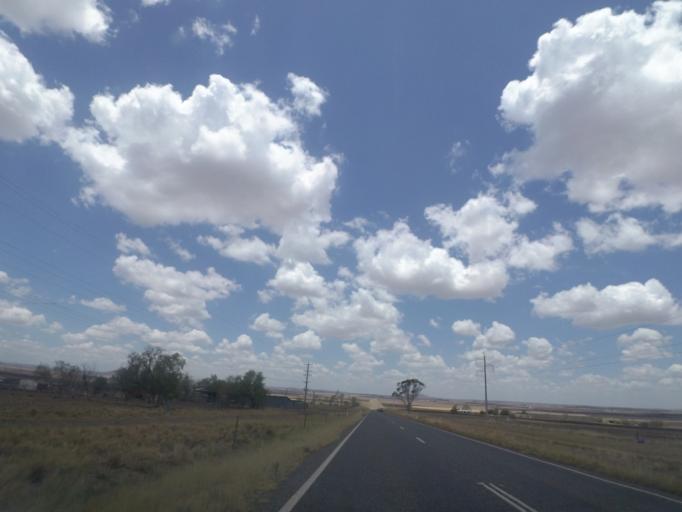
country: AU
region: Queensland
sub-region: Toowoomba
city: Top Camp
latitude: -27.8875
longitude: 151.9720
